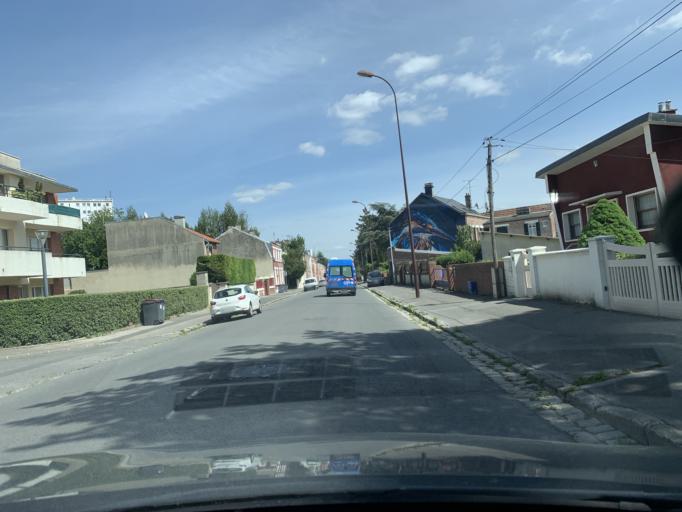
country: FR
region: Picardie
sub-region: Departement de l'Aisne
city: Saint-Quentin
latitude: 49.8582
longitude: 3.3005
